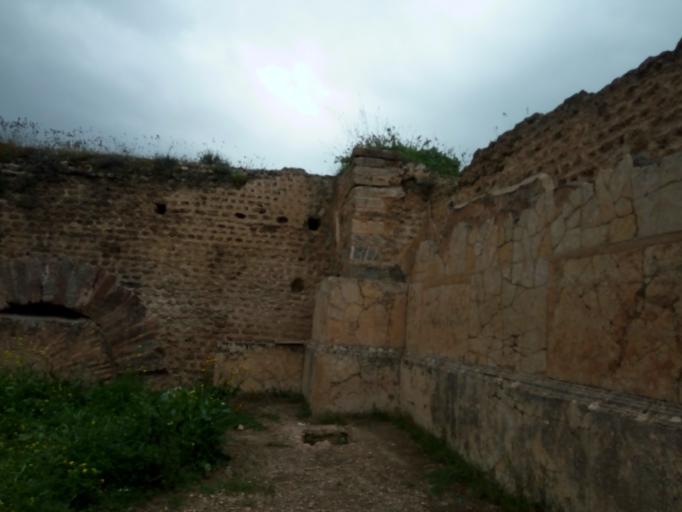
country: DZ
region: Setif
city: El Eulma
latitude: 36.3192
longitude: 5.7362
